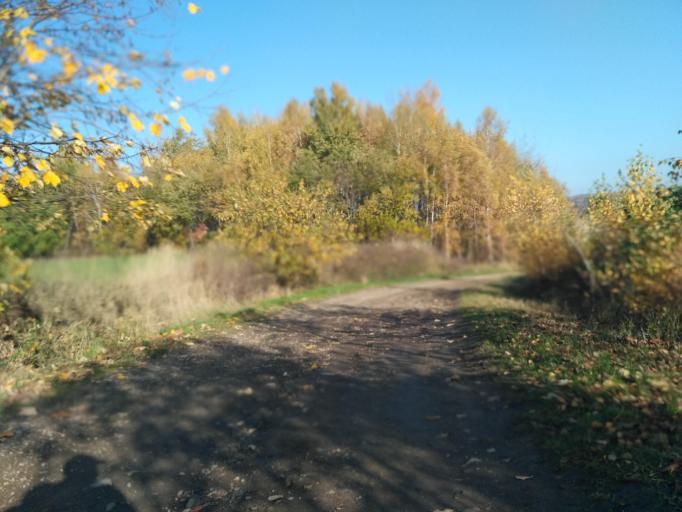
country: PL
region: Subcarpathian Voivodeship
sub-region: Powiat rzeszowski
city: Blazowa
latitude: 49.8665
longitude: 22.0847
